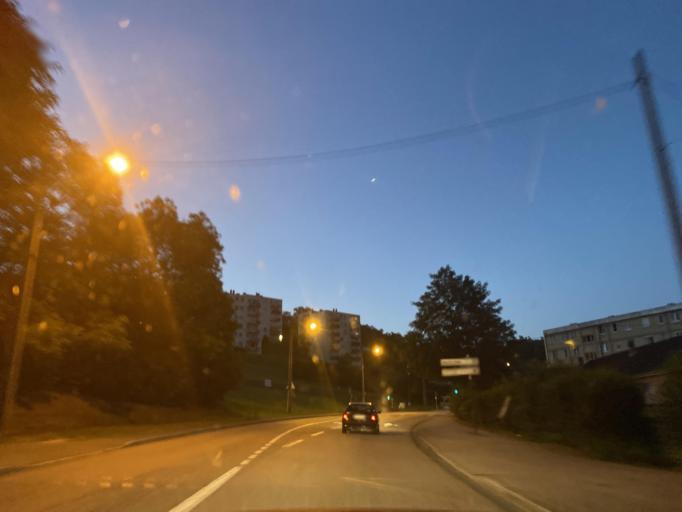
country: FR
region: Haute-Normandie
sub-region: Departement de l'Eure
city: Evreux
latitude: 49.0292
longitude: 1.1655
